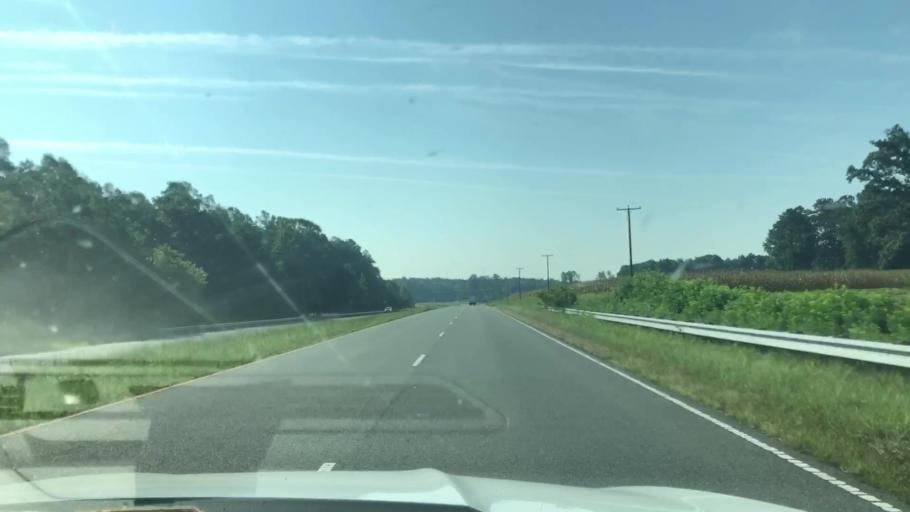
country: US
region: Virginia
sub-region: Richmond County
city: Warsaw
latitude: 37.9124
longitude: -76.6962
